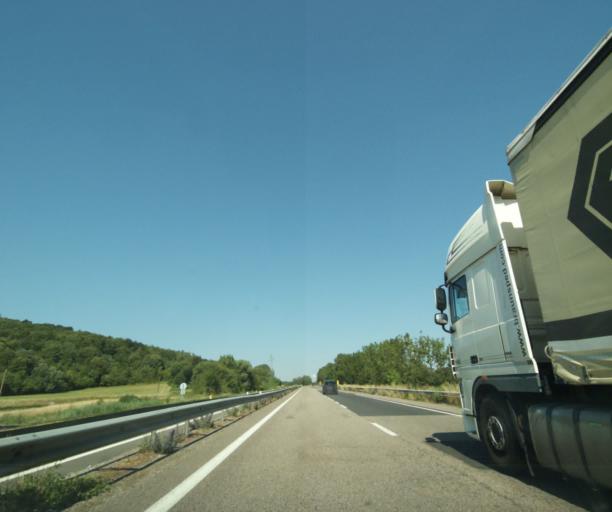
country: FR
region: Lorraine
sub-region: Departement de Meurthe-et-Moselle
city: Foug
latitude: 48.6694
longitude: 5.8079
